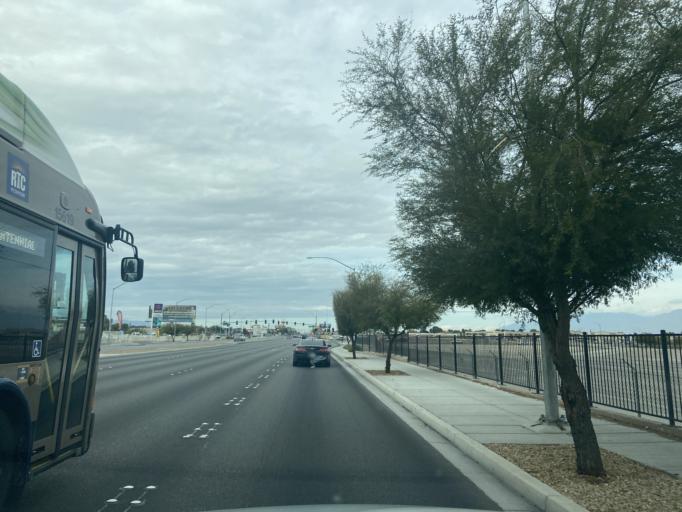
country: US
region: Nevada
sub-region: Clark County
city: Las Vegas
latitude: 36.2118
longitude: -115.2070
